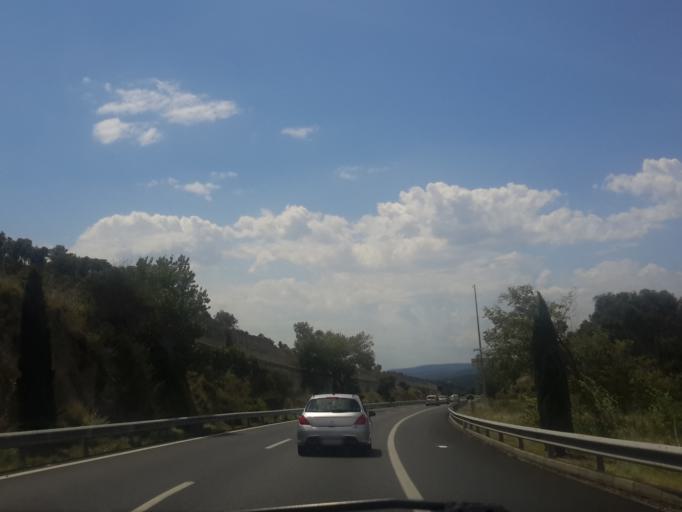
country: ES
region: Catalonia
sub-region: Provincia de Girona
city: la Jonquera
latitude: 42.4504
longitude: 2.8681
